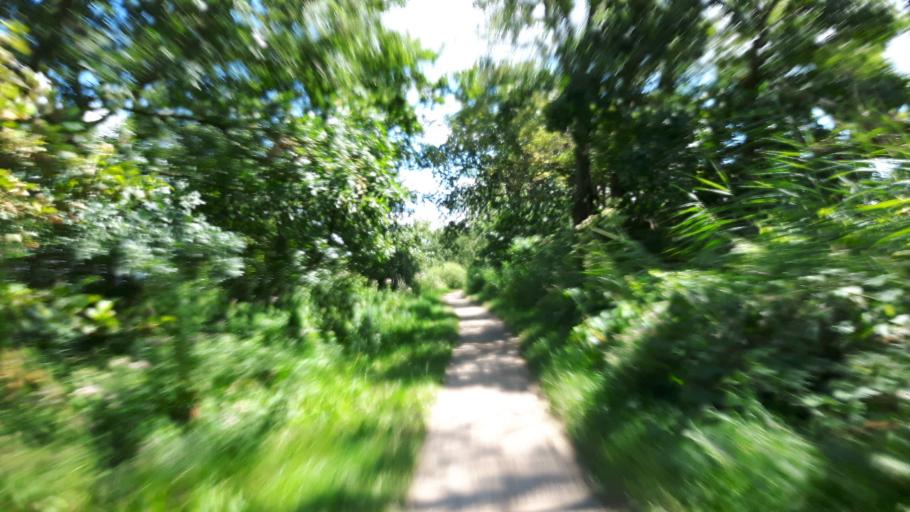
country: NL
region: Utrecht
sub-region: Stichtse Vecht
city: Vreeland
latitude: 52.2214
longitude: 5.0505
